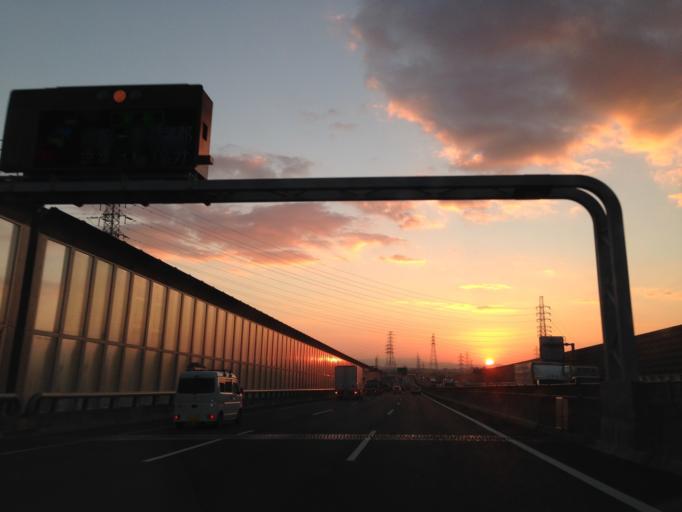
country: JP
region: Aichi
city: Obu
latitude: 35.0431
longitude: 136.9927
